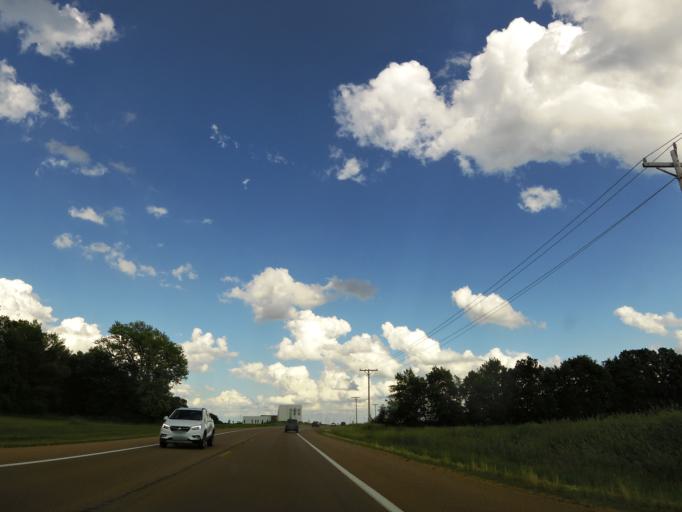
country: US
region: Minnesota
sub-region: Carver County
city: Waconia
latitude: 44.8291
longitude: -93.7514
